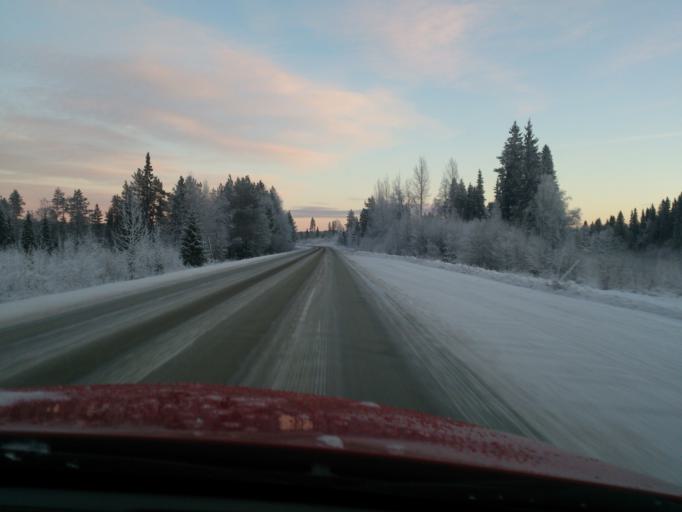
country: SE
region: Jaemtland
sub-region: Harjedalens Kommun
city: Sveg
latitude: 62.4115
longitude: 13.5776
